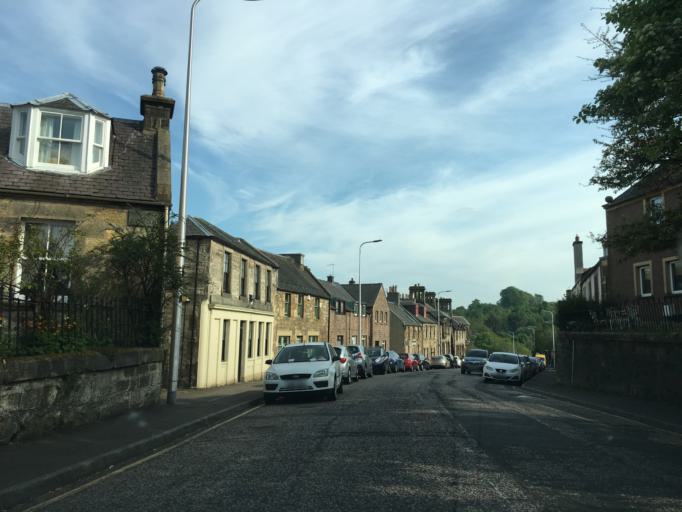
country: GB
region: Scotland
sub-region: Midlothian
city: Penicuik
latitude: 55.8255
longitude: -3.2220
